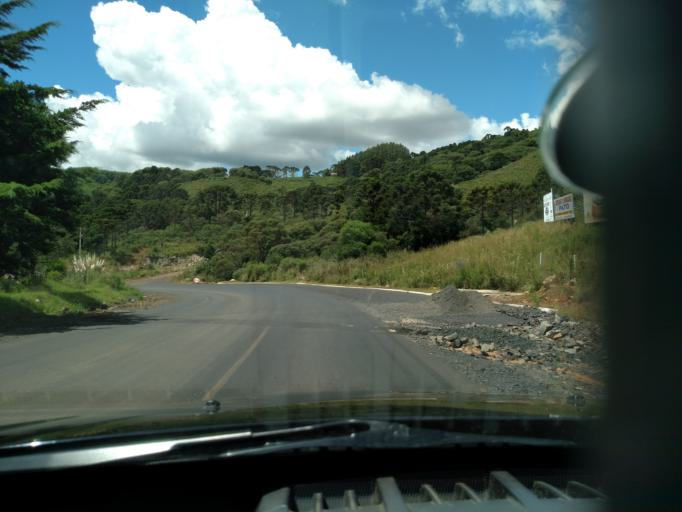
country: BR
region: Santa Catarina
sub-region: Sao Joaquim
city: Sao Joaquim
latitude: -28.2767
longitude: -49.9570
